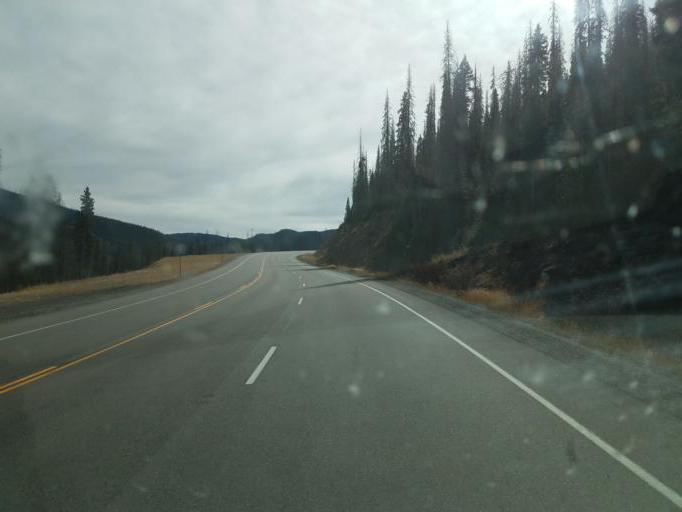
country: US
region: Colorado
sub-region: Archuleta County
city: Pagosa Springs
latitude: 37.4994
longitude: -106.7699
